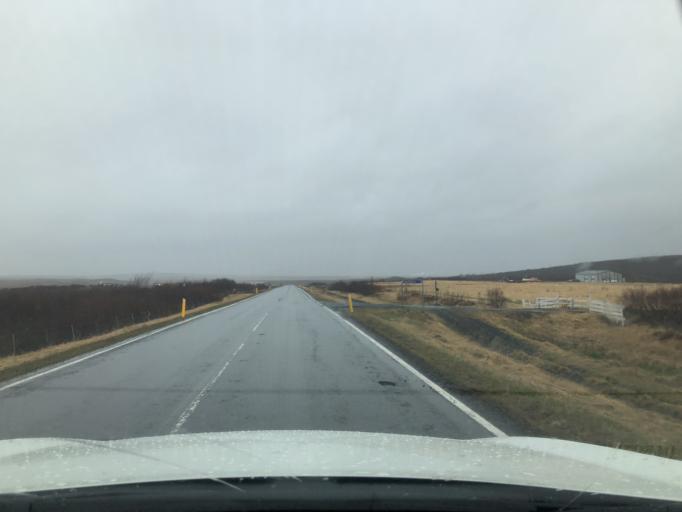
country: IS
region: South
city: Selfoss
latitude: 64.2636
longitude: -20.4692
